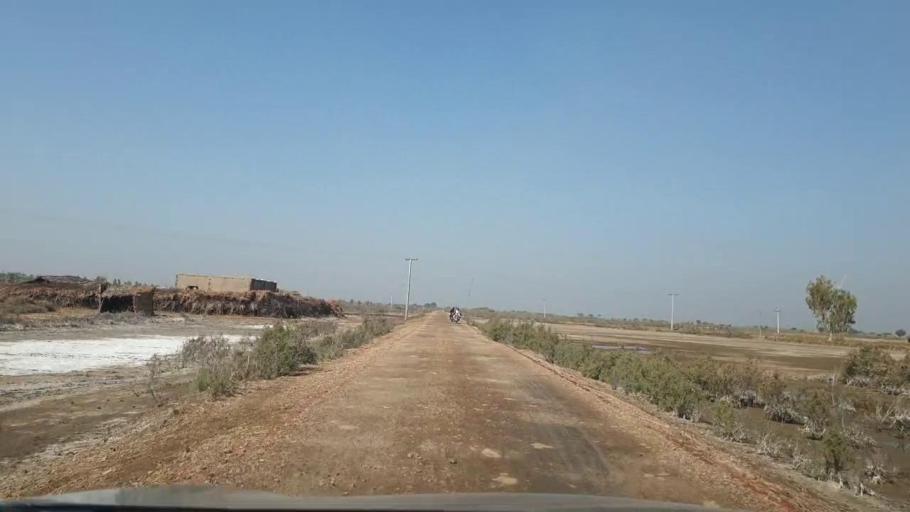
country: PK
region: Sindh
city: Berani
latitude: 25.6878
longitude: 68.8868
